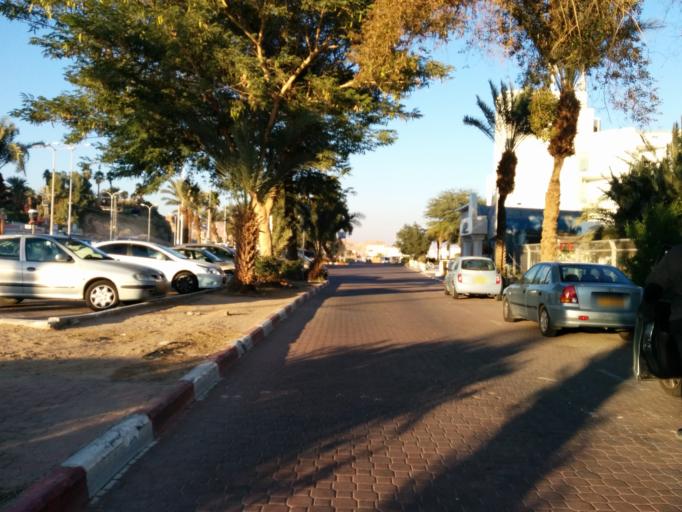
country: IL
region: Southern District
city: Eilat
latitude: 29.5136
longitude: 34.9252
